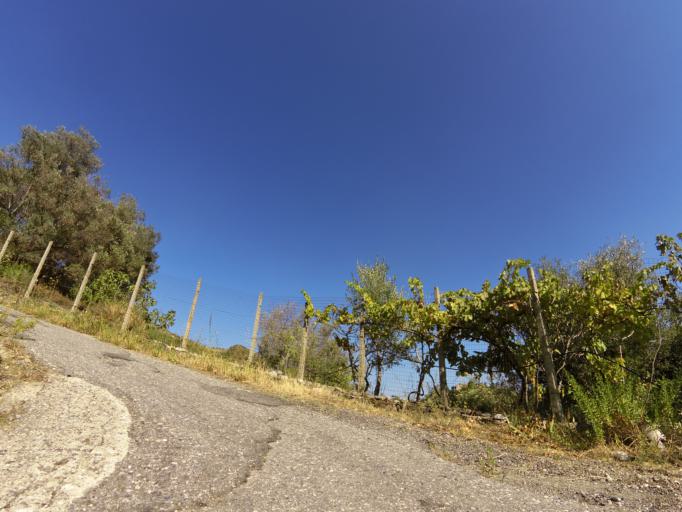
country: IT
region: Calabria
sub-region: Provincia di Reggio Calabria
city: Bivongi
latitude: 38.4921
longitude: 16.4605
